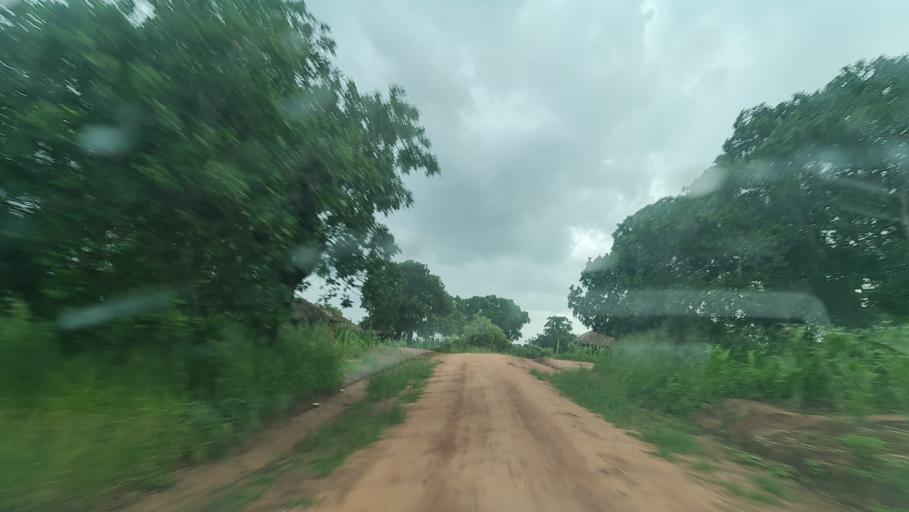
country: MZ
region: Nampula
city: Nacala
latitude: -14.0029
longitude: 40.3573
